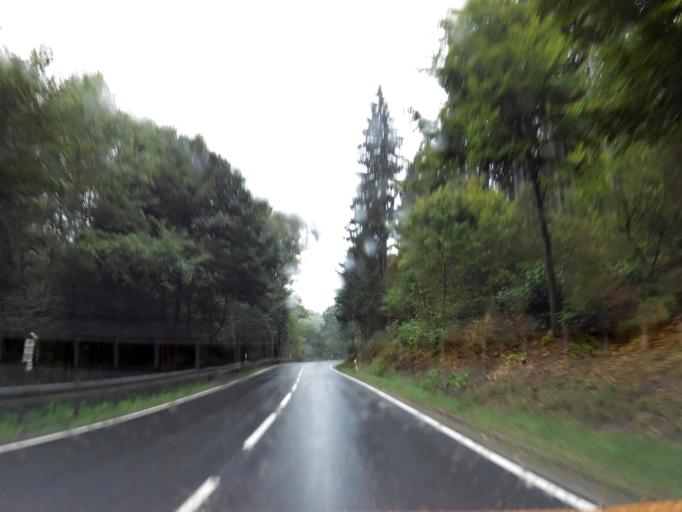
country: DE
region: Saxony-Anhalt
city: Stolberg
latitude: 51.6401
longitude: 10.9681
